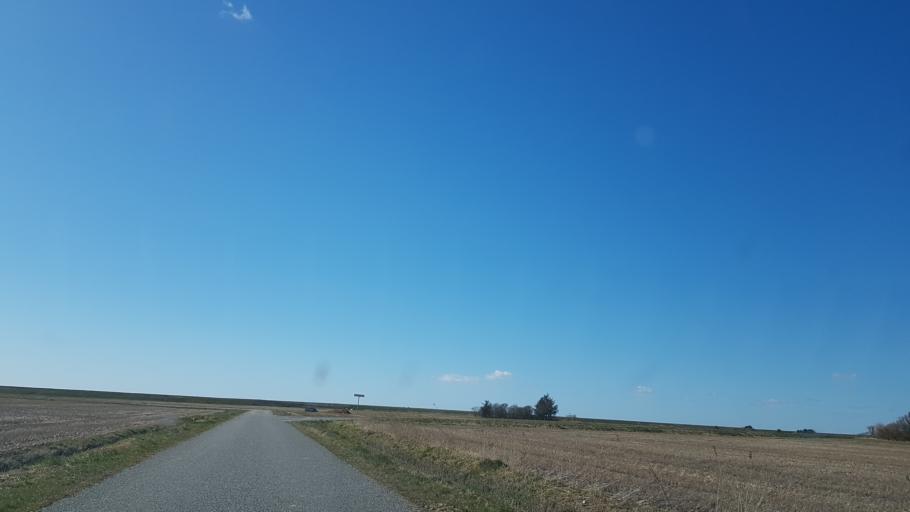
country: DK
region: South Denmark
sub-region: Esbjerg Kommune
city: Ribe
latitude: 55.2577
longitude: 8.6749
